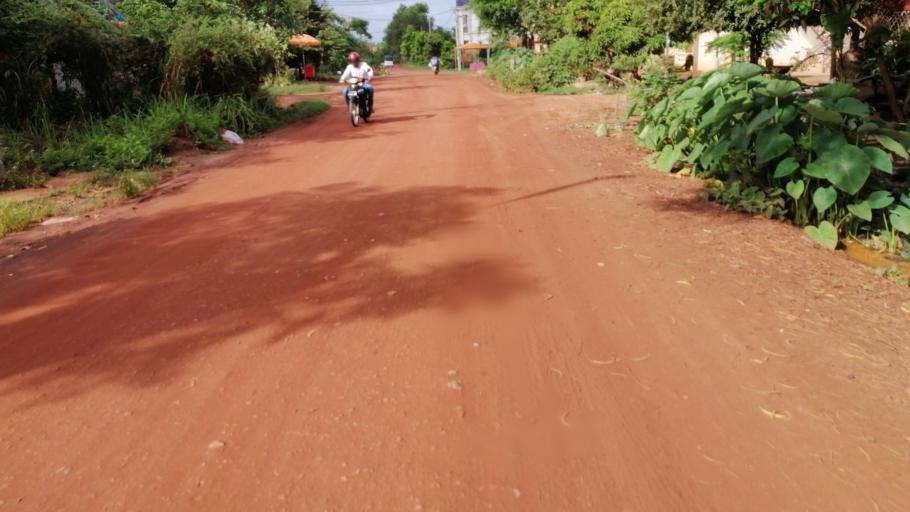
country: KH
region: Siem Reap
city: Siem Reap
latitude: 13.3623
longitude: 103.8304
